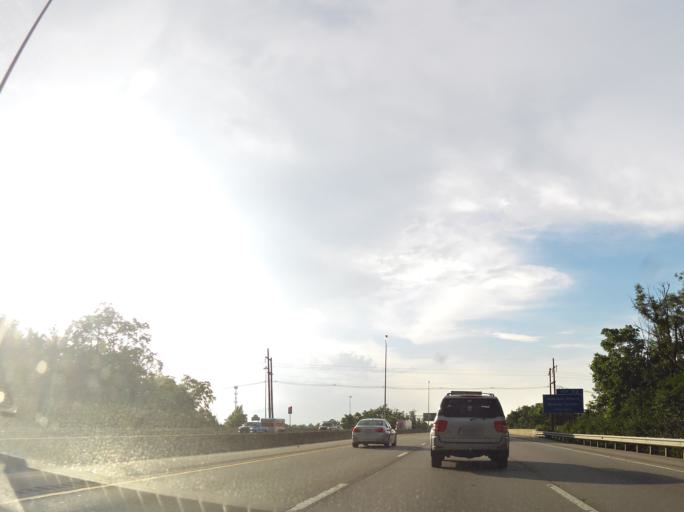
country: US
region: Kentucky
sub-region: Fayette County
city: Lexington-Fayette
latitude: 38.0746
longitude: -84.4547
